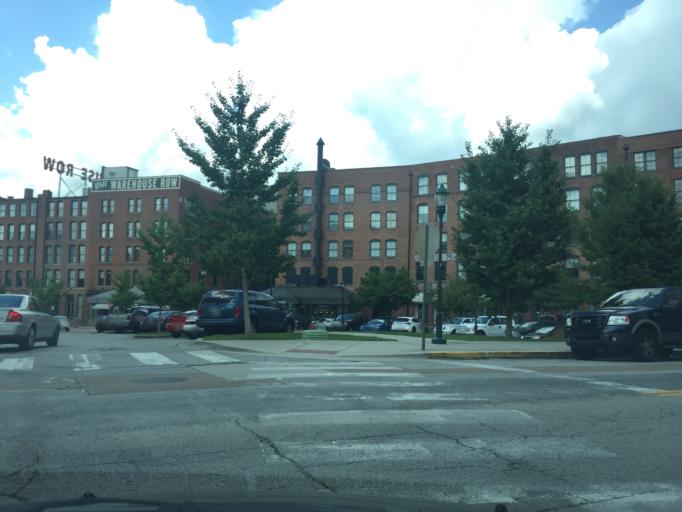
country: US
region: Tennessee
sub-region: Hamilton County
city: Chattanooga
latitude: 35.0435
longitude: -85.3079
